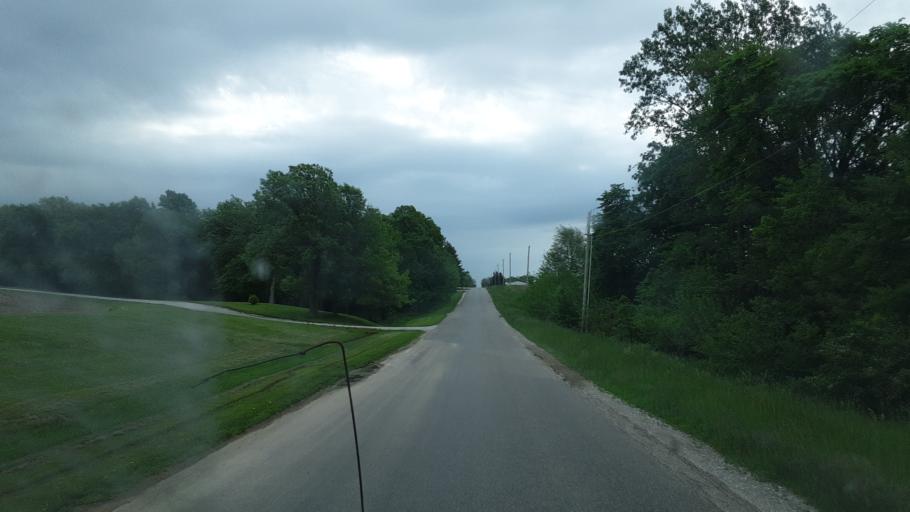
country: US
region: Illinois
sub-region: Fulton County
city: Astoria
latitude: 40.3644
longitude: -90.4390
